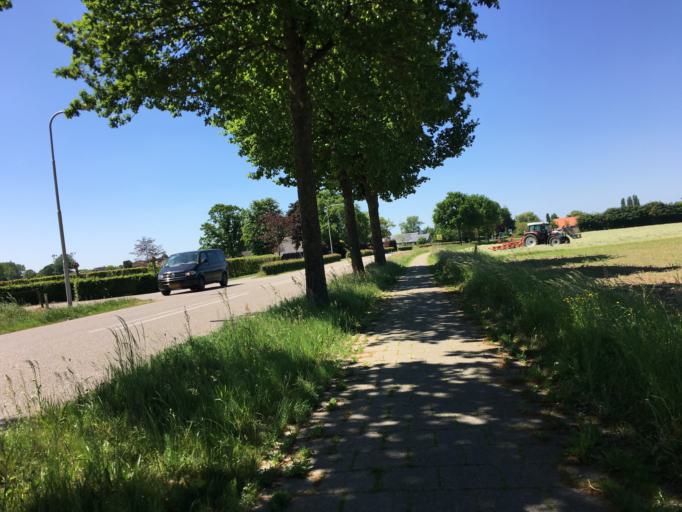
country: NL
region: North Brabant
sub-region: Gemeente Heusden
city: Heusden
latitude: 51.7303
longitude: 5.1643
